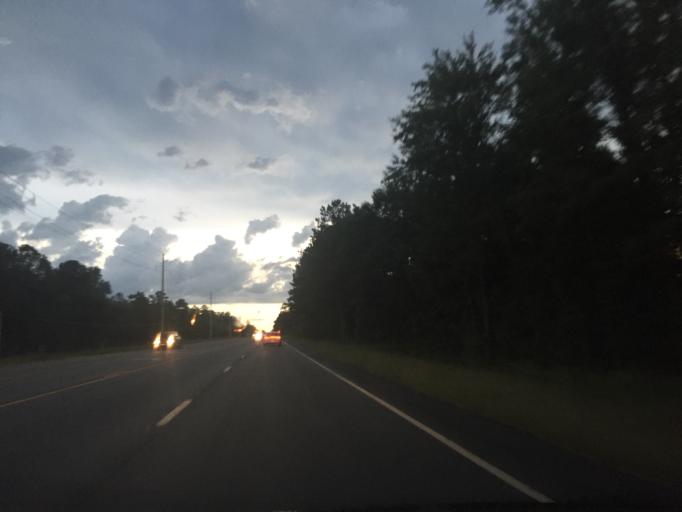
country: US
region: Georgia
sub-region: Liberty County
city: Hinesville
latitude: 31.8525
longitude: -81.5554
